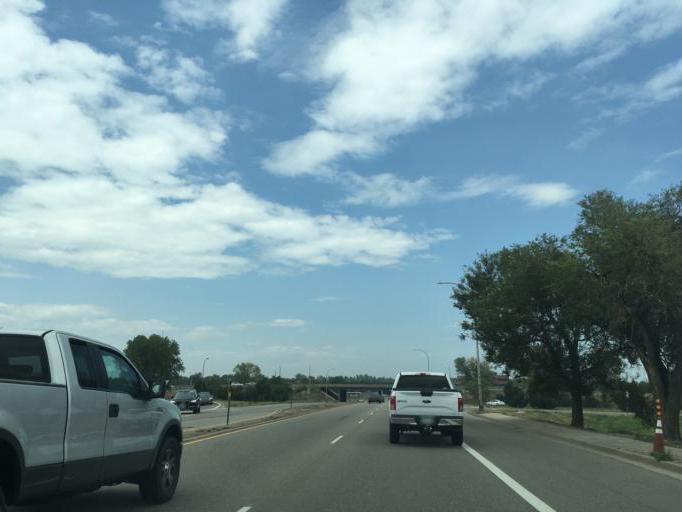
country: US
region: Colorado
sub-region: Jefferson County
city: Lakewood
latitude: 39.7229
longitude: -105.1096
